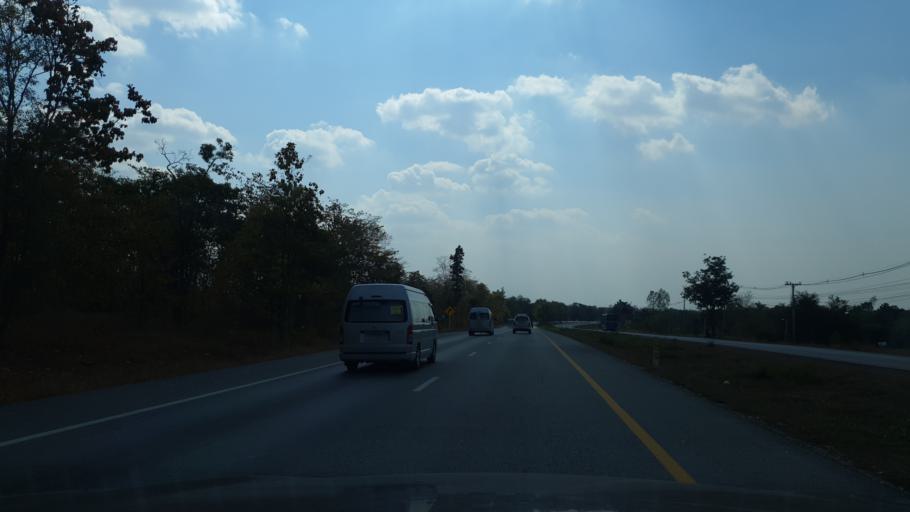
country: TH
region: Tak
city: Sam Ngao
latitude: 17.3073
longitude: 99.1484
